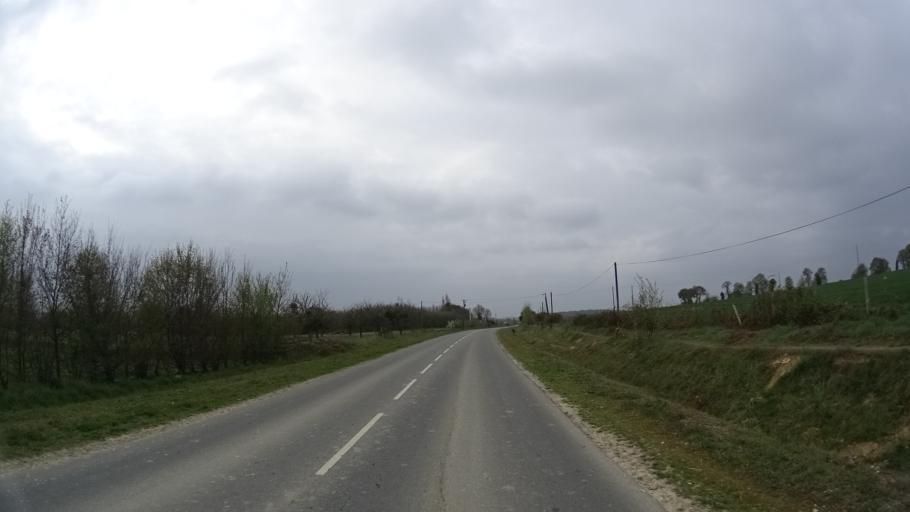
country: FR
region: Brittany
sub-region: Departement d'Ille-et-Vilaine
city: La Chapelle-Thouarault
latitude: 48.1265
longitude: -1.8546
